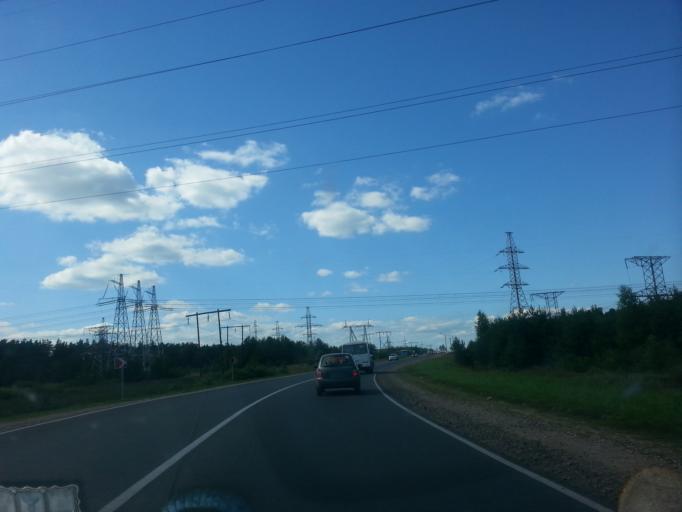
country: RU
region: Nizjnij Novgorod
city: Lukino
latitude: 56.3894
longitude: 43.6988
